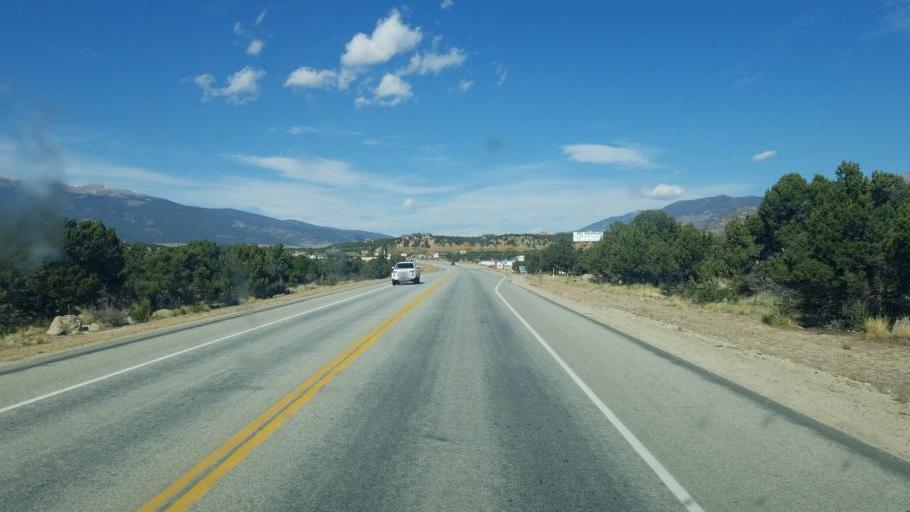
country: US
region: Colorado
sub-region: Chaffee County
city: Buena Vista
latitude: 38.8557
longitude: -106.1411
